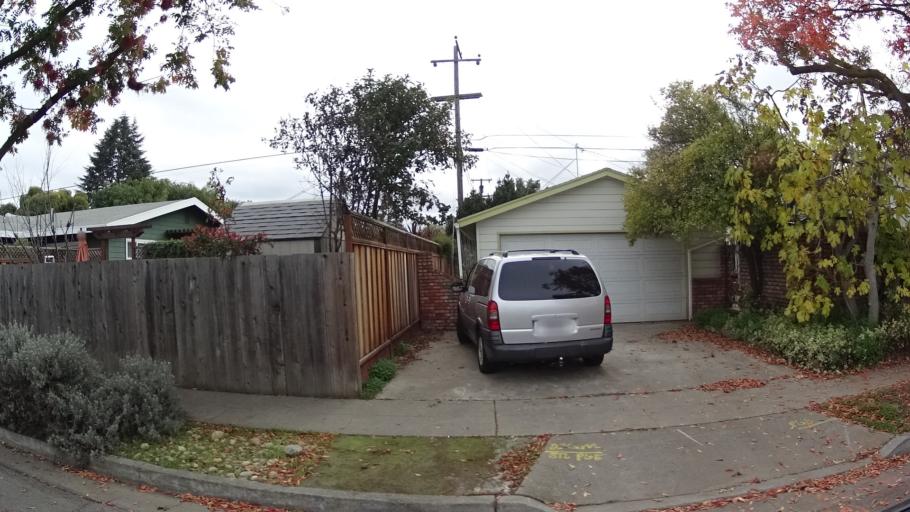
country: US
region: California
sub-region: Santa Clara County
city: Sunnyvale
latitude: 37.3708
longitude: -122.0516
